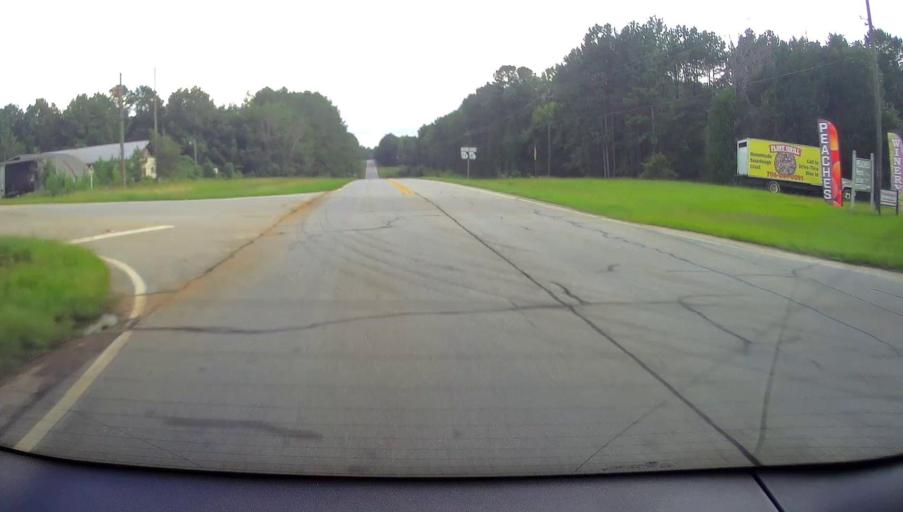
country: US
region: Georgia
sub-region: Meriwether County
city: Greenville
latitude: 33.0366
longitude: -84.5646
